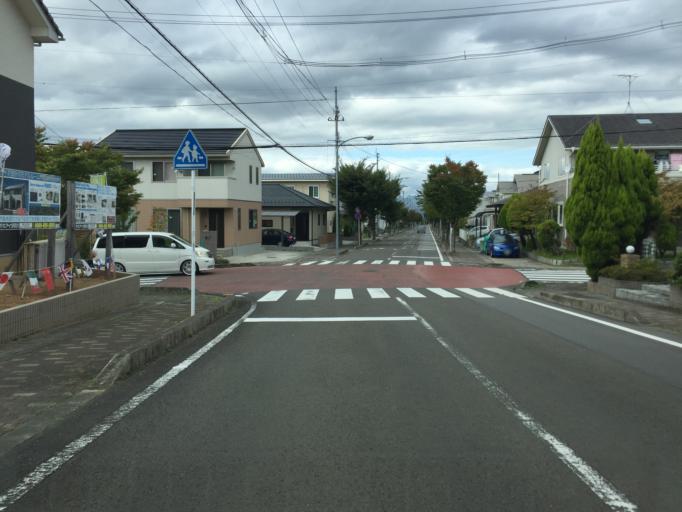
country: JP
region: Fukushima
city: Fukushima-shi
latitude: 37.7116
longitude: 140.4725
